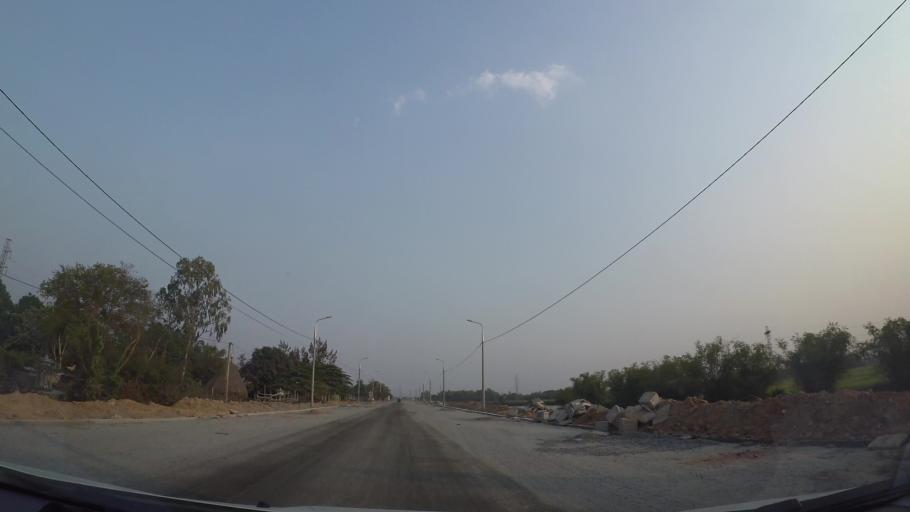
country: VN
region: Da Nang
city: Ngu Hanh Son
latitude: 15.9602
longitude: 108.2322
